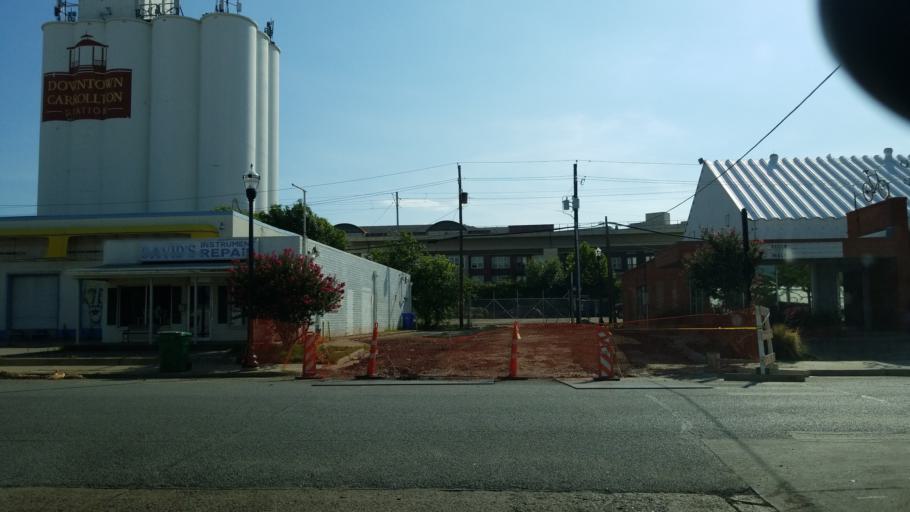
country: US
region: Texas
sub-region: Dallas County
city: Carrollton
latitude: 32.9512
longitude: -96.9073
